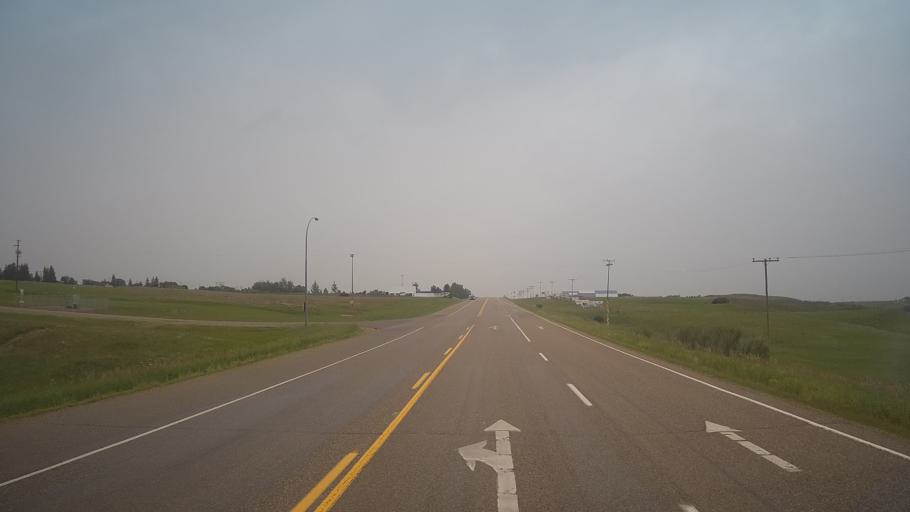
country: CA
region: Saskatchewan
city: Biggar
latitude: 52.0593
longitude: -107.9643
